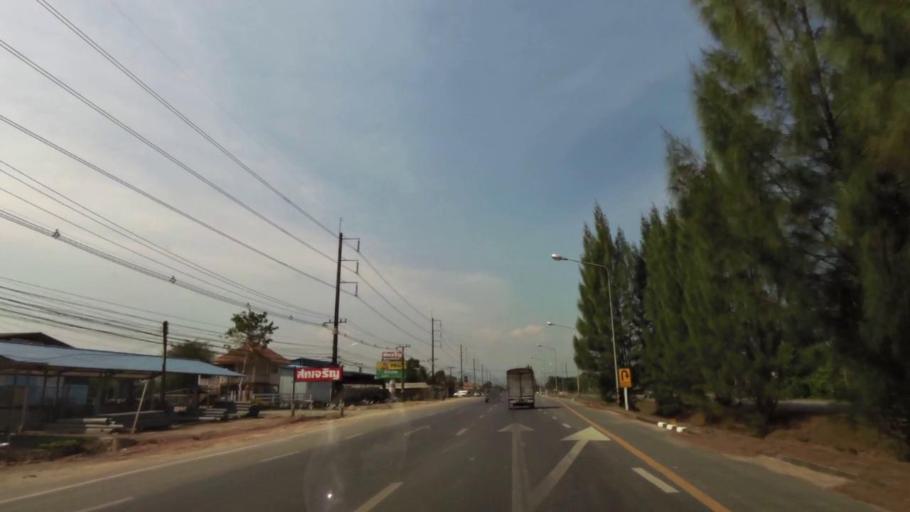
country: TH
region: Chanthaburi
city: Chanthaburi
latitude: 12.6284
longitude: 102.1469
